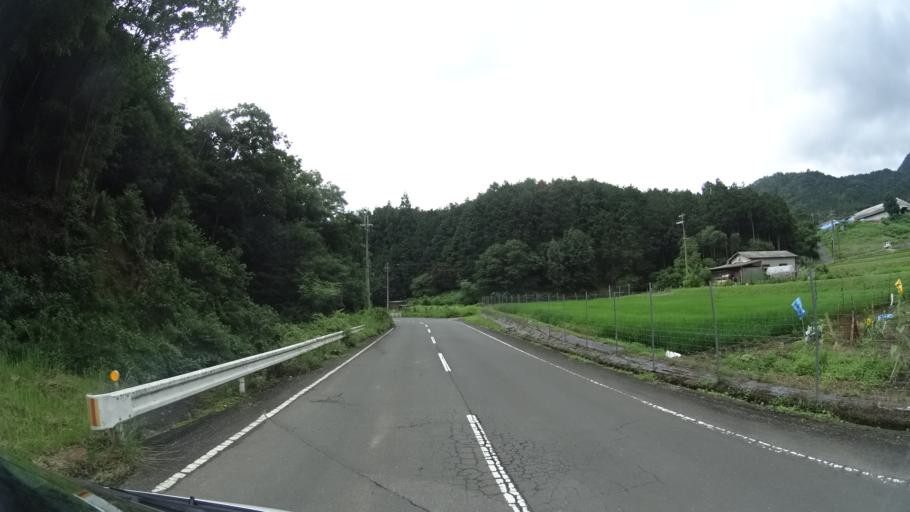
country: JP
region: Kyoto
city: Kameoka
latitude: 35.0889
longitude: 135.4365
